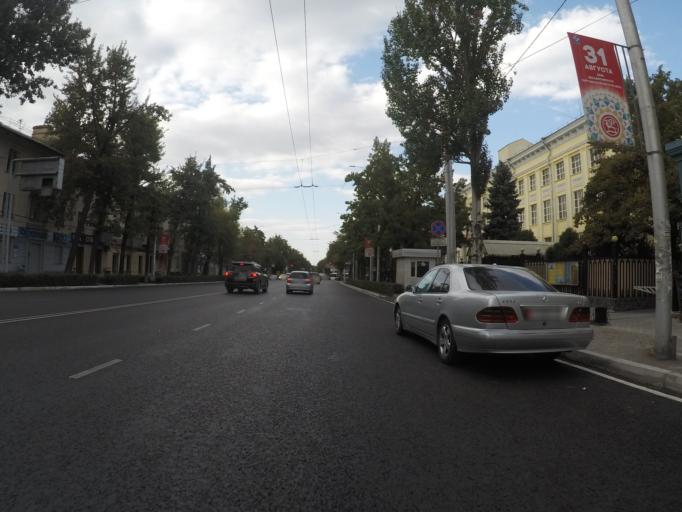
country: KG
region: Chuy
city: Bishkek
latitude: 42.8745
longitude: 74.5882
